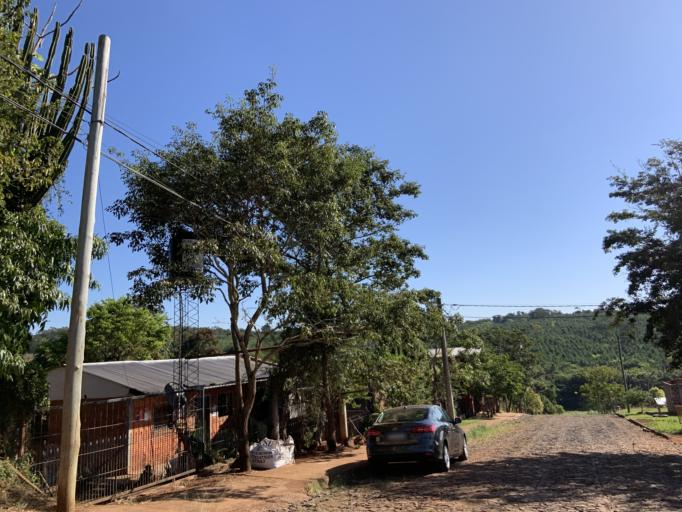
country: AR
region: Misiones
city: Puerto Rico
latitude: -26.8065
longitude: -55.0362
